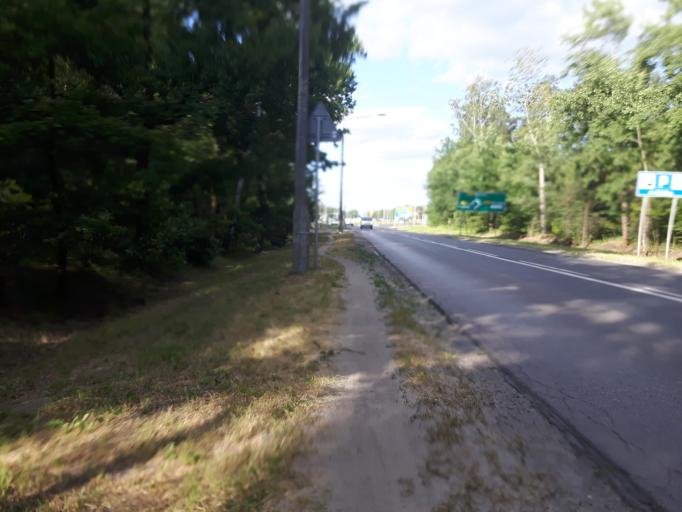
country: PL
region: Masovian Voivodeship
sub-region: Powiat wolominski
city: Zabki
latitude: 52.2928
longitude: 21.1338
